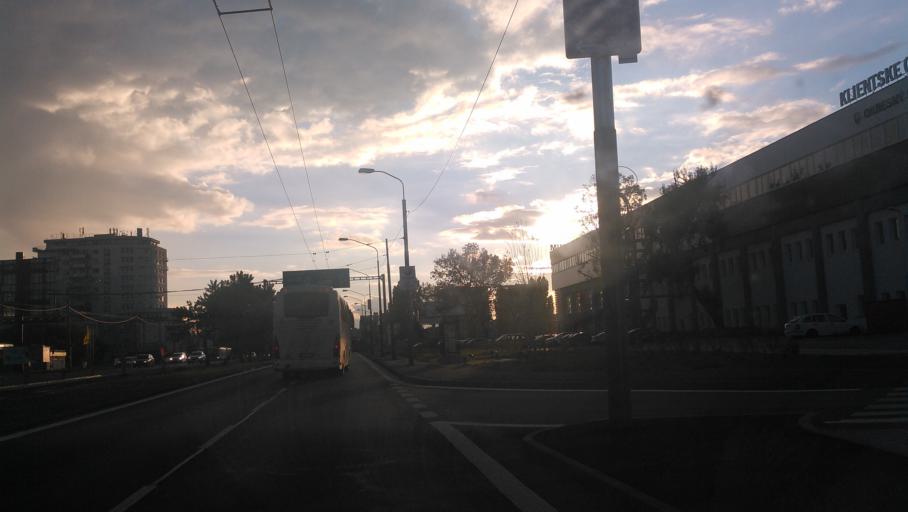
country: SK
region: Bratislavsky
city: Bratislava
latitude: 48.1666
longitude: 17.1533
